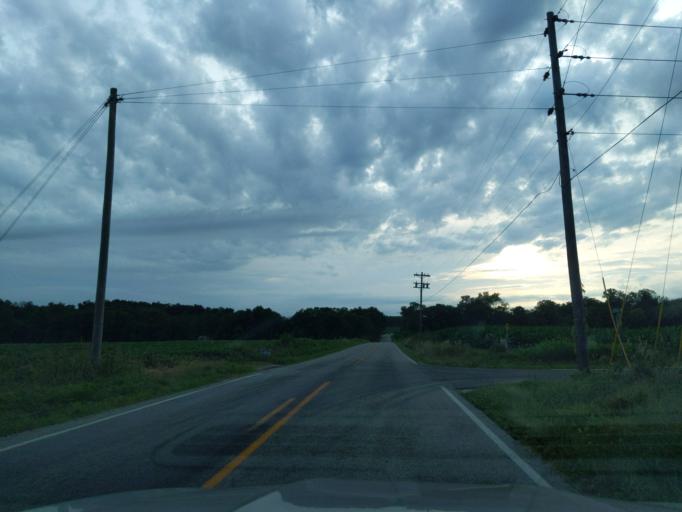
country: US
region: Indiana
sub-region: Ripley County
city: Osgood
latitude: 39.1982
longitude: -85.2963
